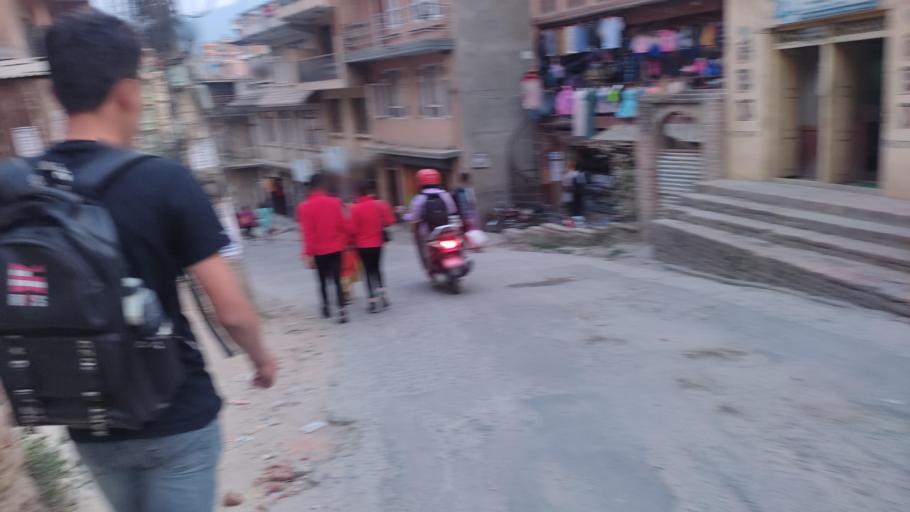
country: NP
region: Central Region
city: Kirtipur
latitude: 27.6740
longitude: 85.2801
